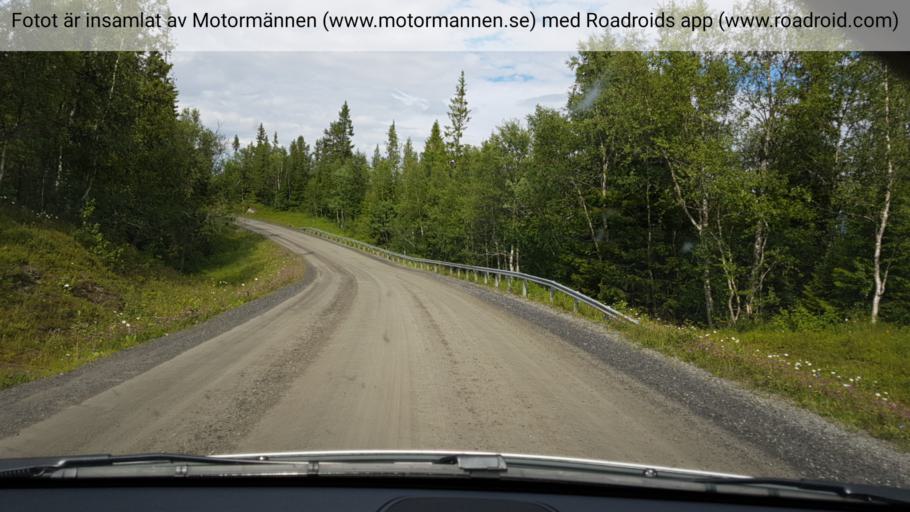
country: NO
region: Nord-Trondelag
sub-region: Snasa
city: Snaase
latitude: 63.7169
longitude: 12.4819
